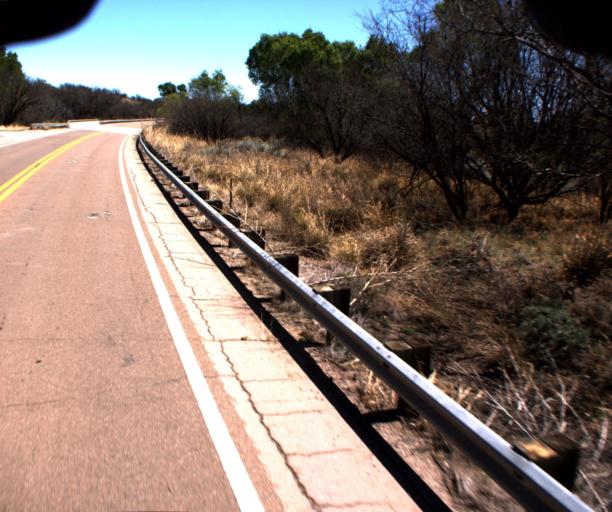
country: US
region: Arizona
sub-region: Pima County
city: Corona de Tucson
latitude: 31.6540
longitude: -110.7127
